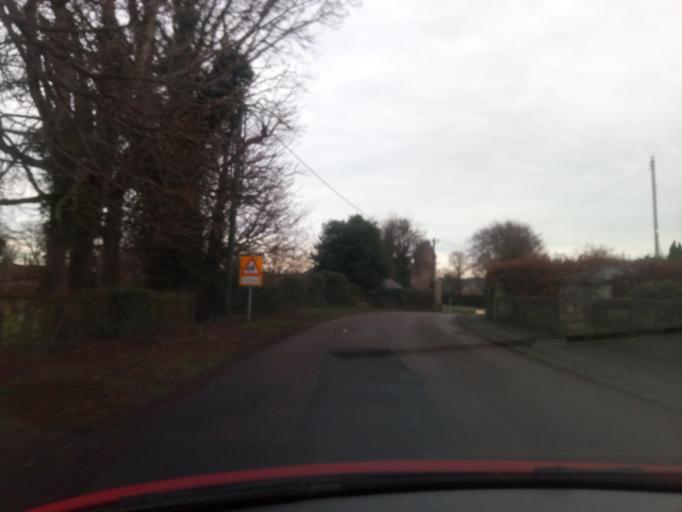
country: GB
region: England
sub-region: Northumberland
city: Wooler
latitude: 55.5480
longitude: -2.0211
